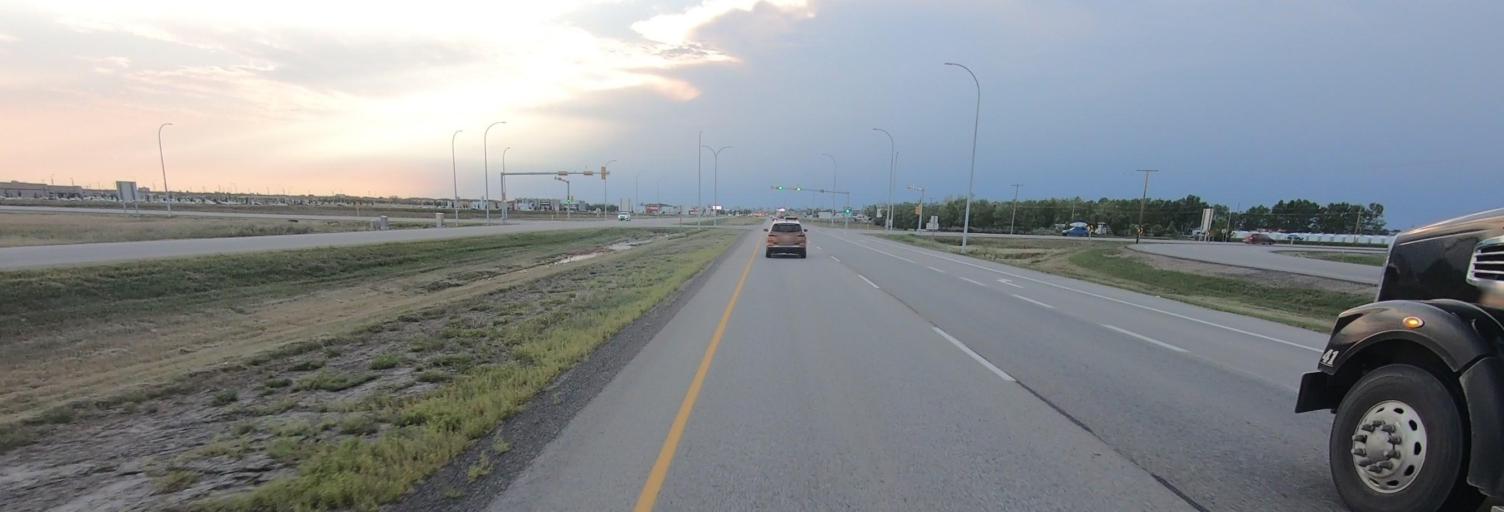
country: CA
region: Saskatchewan
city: Pilot Butte
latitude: 50.4478
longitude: -104.5015
